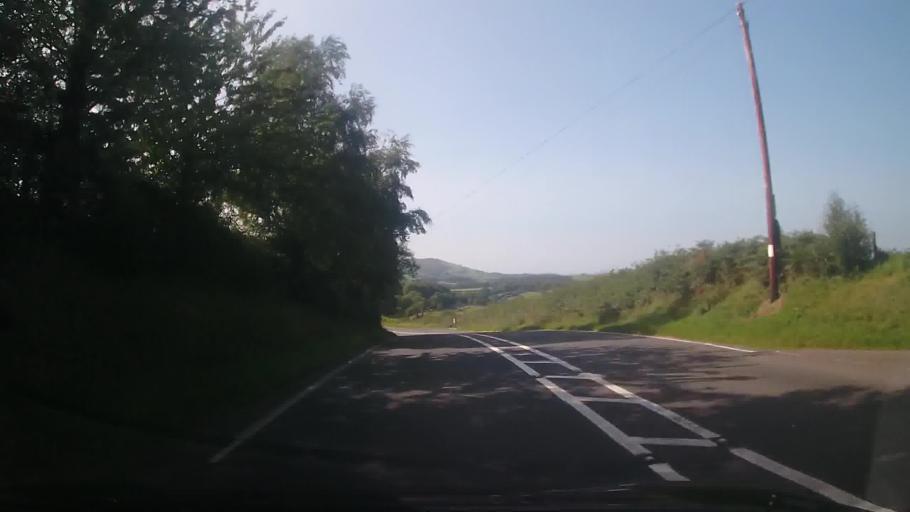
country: GB
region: Wales
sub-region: Sir Powys
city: Builth Wells
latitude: 52.1501
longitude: -3.4661
